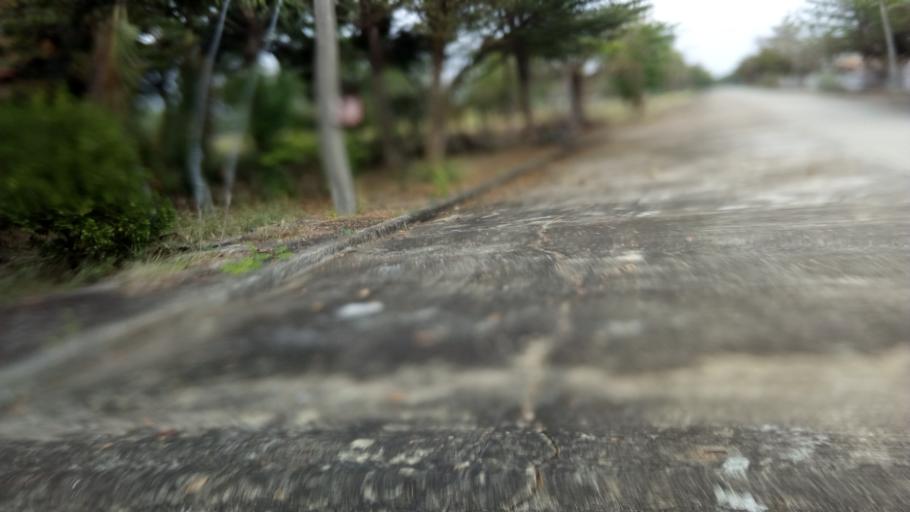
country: TH
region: Sara Buri
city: Nong Khae
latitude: 14.2489
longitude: 100.8322
